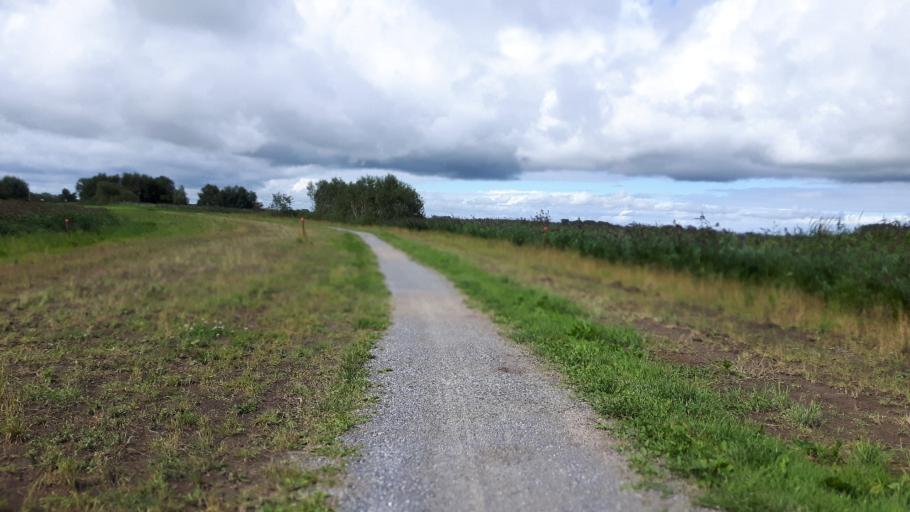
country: NL
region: Groningen
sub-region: Gemeente Slochteren
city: Slochteren
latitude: 53.2685
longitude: 6.8185
